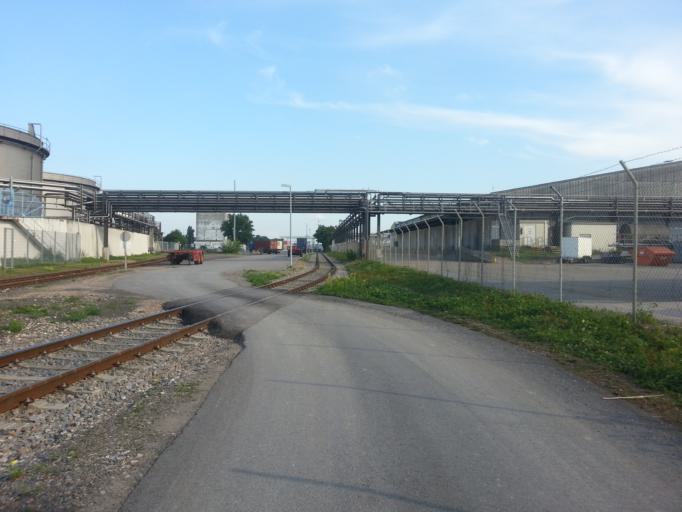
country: DE
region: Rheinland-Pfalz
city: Ludwigshafen am Rhein
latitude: 49.5083
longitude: 8.4402
